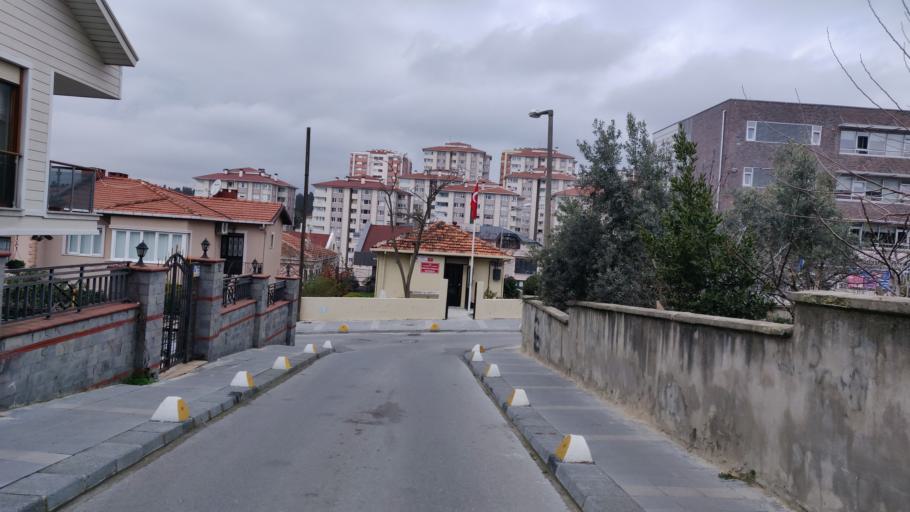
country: TR
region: Istanbul
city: UEskuedar
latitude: 41.0088
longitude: 29.0361
